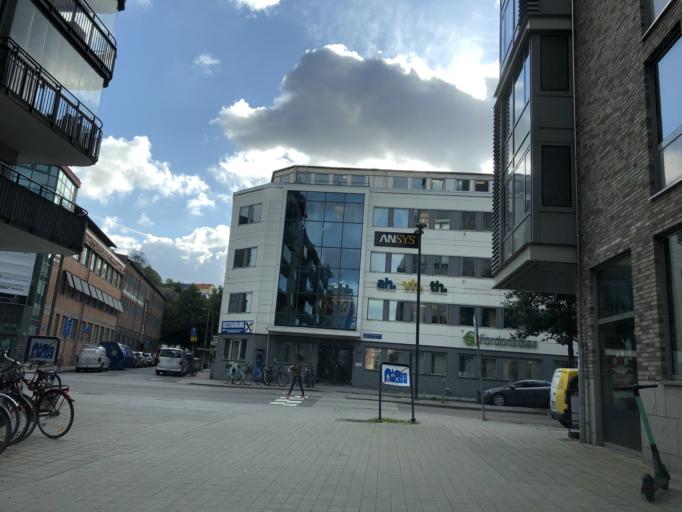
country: SE
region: Vaestra Goetaland
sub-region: Goteborg
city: Goeteborg
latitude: 57.7105
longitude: 11.9943
